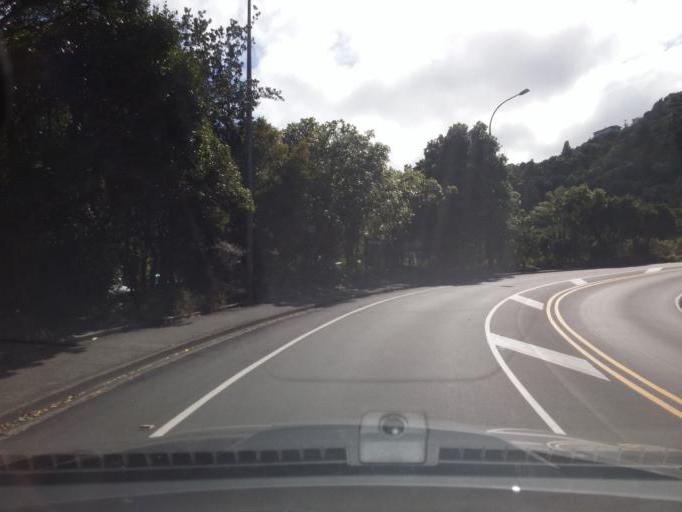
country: NZ
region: Wellington
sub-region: Wellington City
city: Kelburn
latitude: -41.2575
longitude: 174.7797
